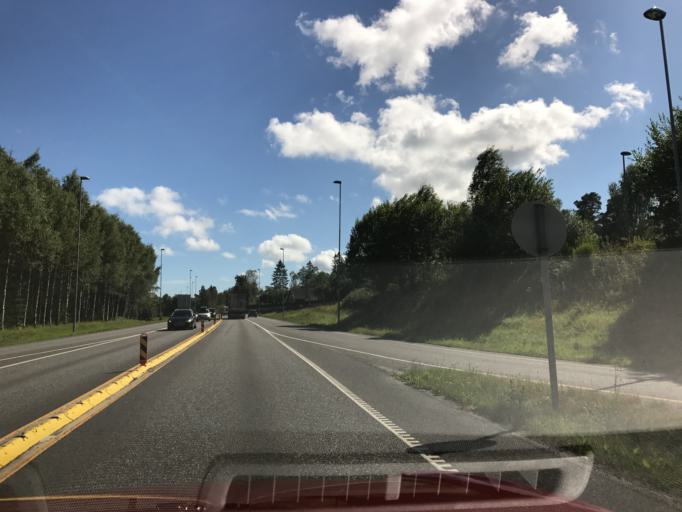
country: NO
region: Telemark
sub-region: Bamble
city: Langesund
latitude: 59.0349
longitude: 9.6765
